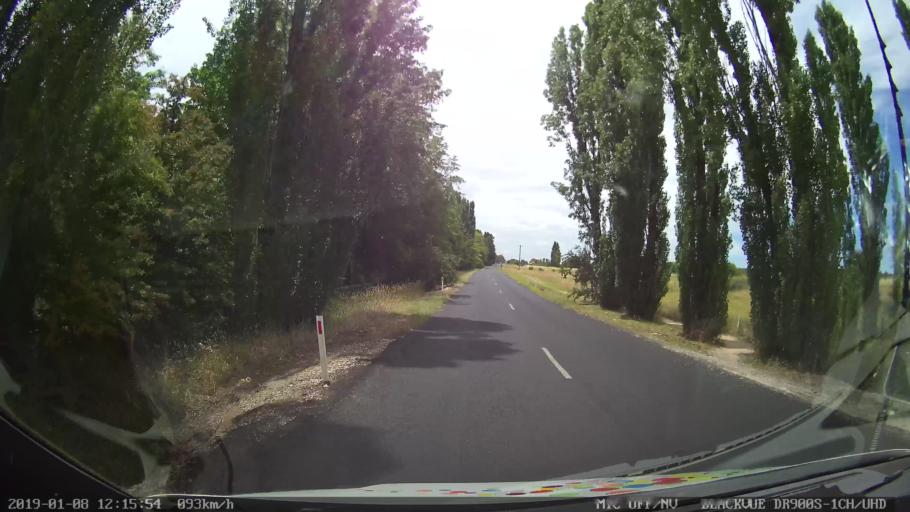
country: AU
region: New South Wales
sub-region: Armidale Dumaresq
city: Armidale
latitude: -30.4936
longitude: 151.6307
